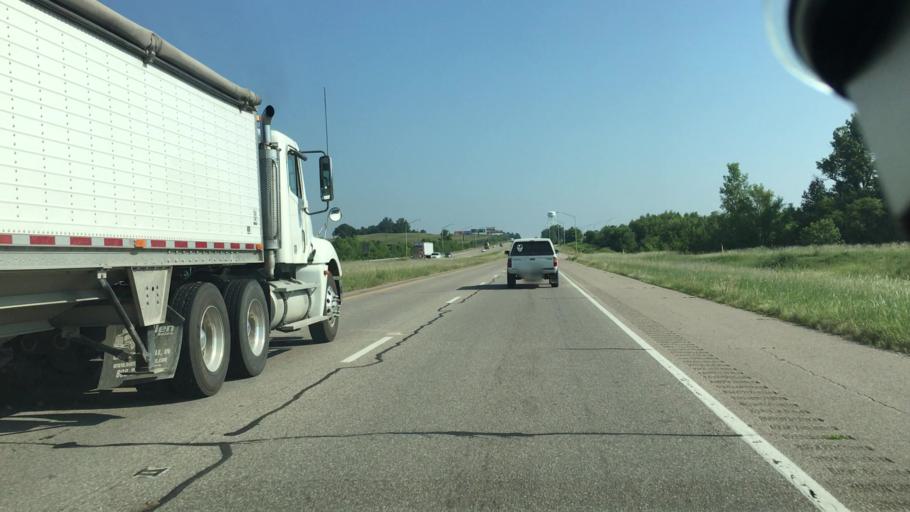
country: US
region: Indiana
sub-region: Gibson County
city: Fort Branch
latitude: 38.2760
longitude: -87.5676
